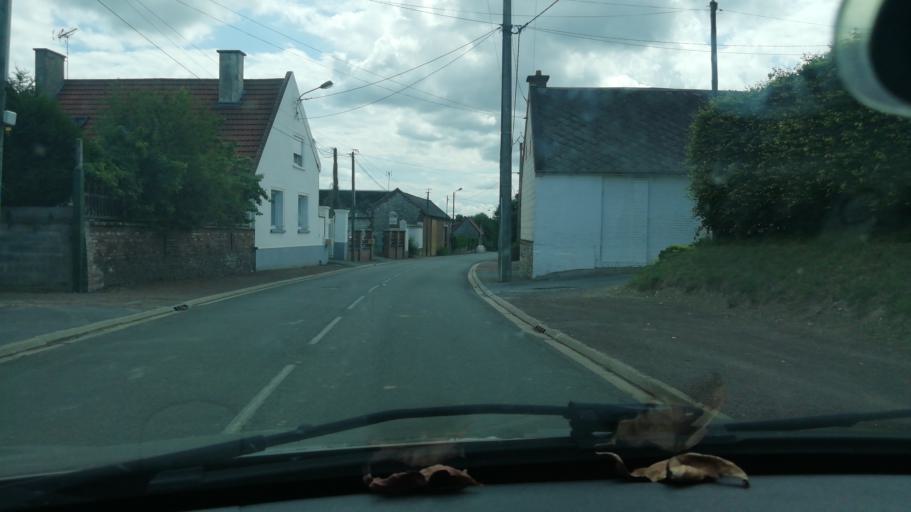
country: FR
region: Nord-Pas-de-Calais
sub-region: Departement du Pas-de-Calais
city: Aubigny-en-Artois
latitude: 50.3259
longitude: 2.5877
